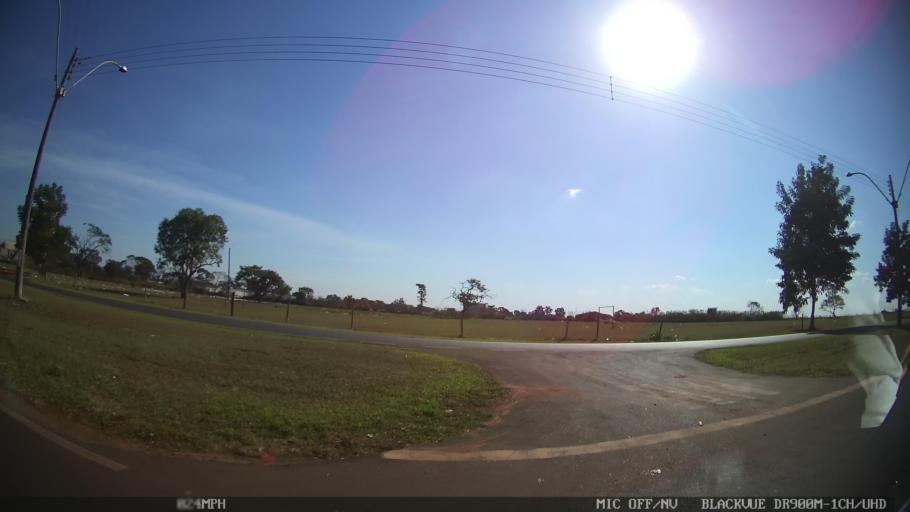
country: BR
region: Sao Paulo
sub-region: Ribeirao Preto
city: Ribeirao Preto
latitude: -21.1482
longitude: -47.7709
